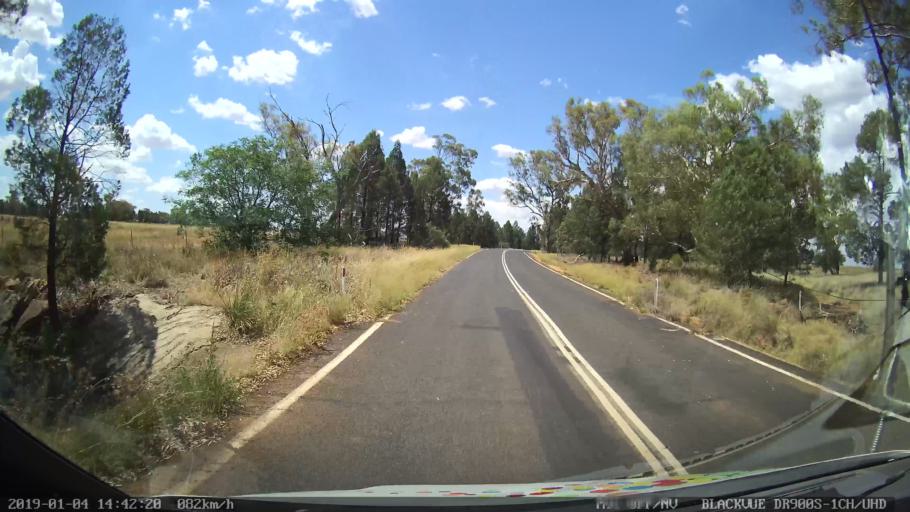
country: AU
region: New South Wales
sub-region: Dubbo Municipality
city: Dubbo
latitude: -32.1292
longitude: 148.6414
